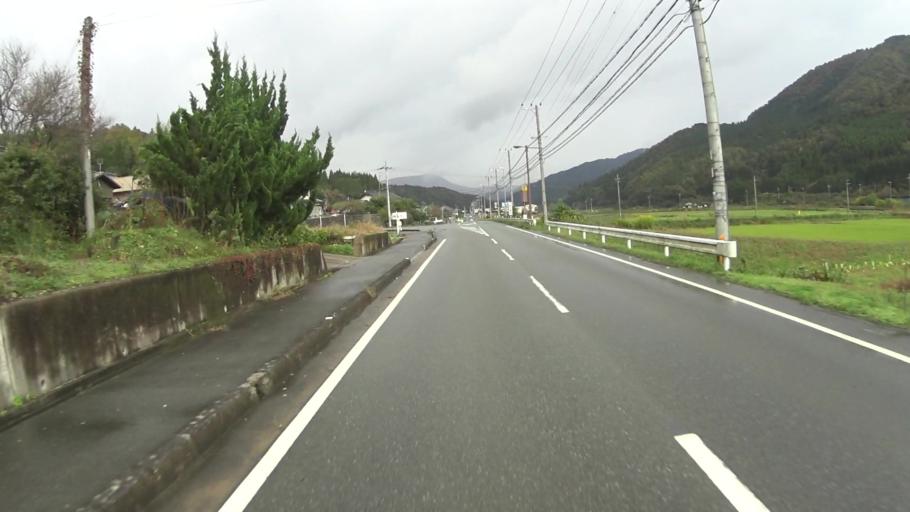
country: JP
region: Kyoto
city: Fukuchiyama
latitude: 35.4037
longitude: 135.1500
